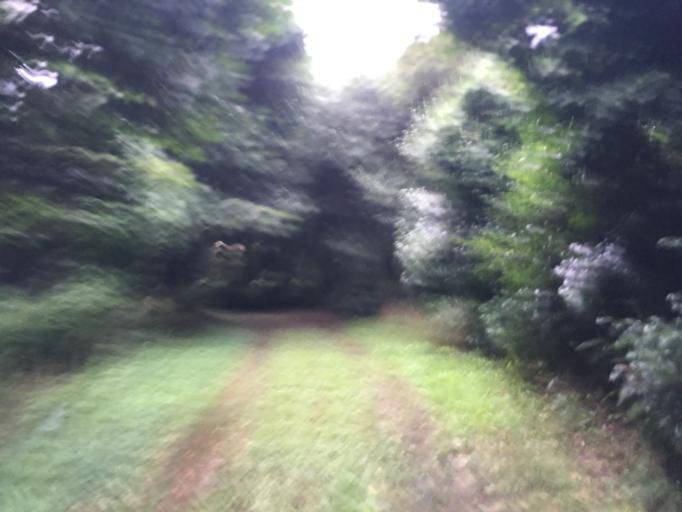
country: JP
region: Aichi
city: Ishiki
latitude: 34.7300
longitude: 137.0439
